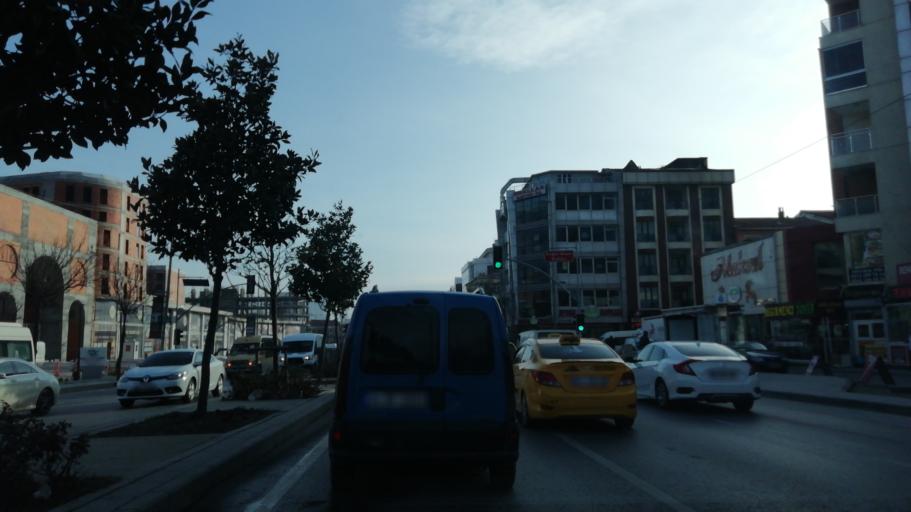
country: TR
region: Istanbul
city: Esenyurt
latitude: 41.0463
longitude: 28.6745
